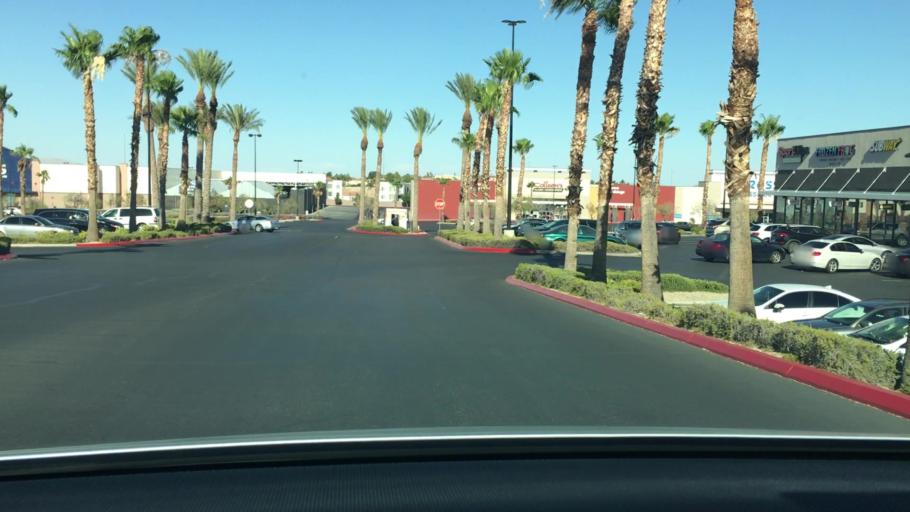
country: US
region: Nevada
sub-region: Clark County
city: Summerlin South
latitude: 36.0963
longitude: -115.2969
